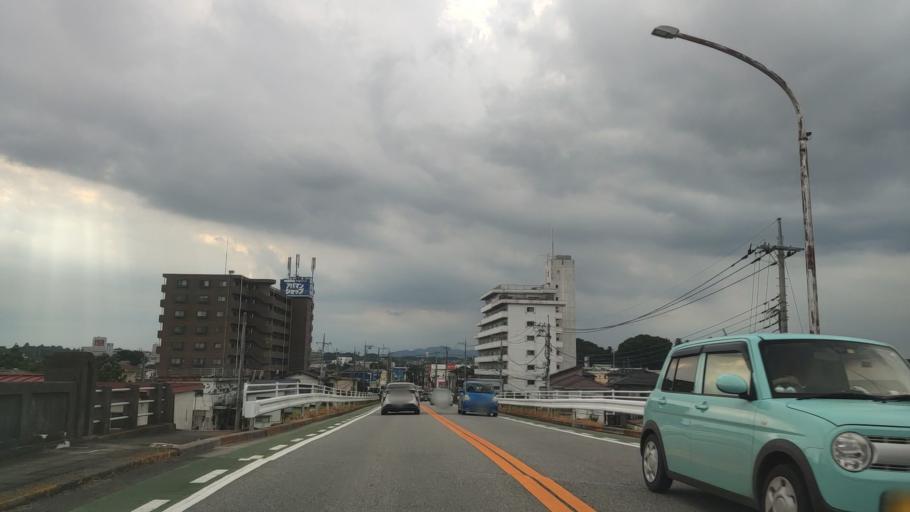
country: JP
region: Tochigi
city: Utsunomiya-shi
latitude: 36.5733
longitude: 139.9075
